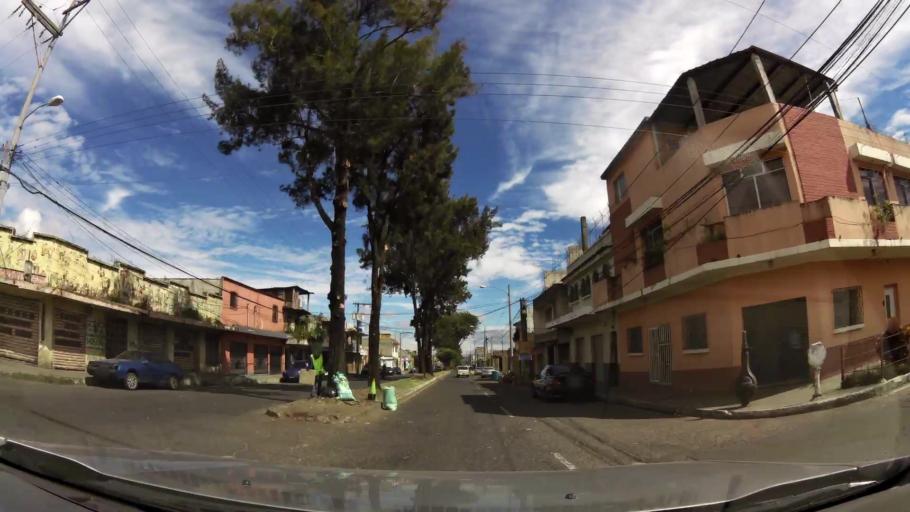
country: GT
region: Guatemala
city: Mixco
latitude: 14.6593
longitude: -90.5785
